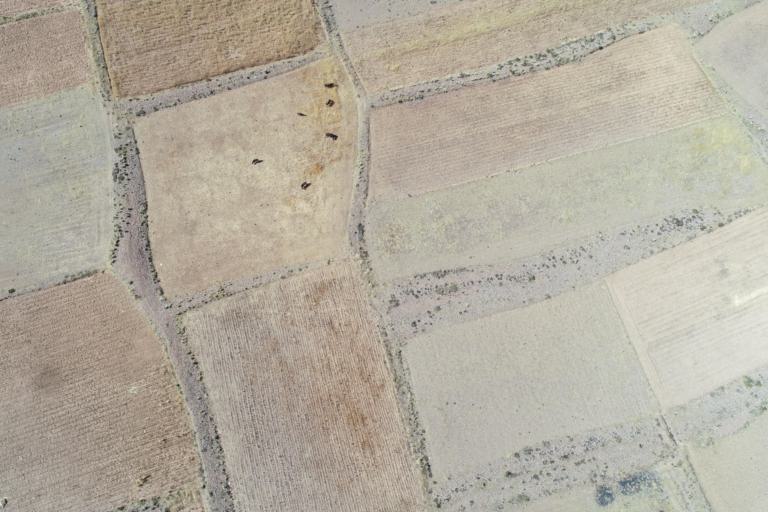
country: BO
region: La Paz
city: Achacachi
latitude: -15.8989
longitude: -68.9001
